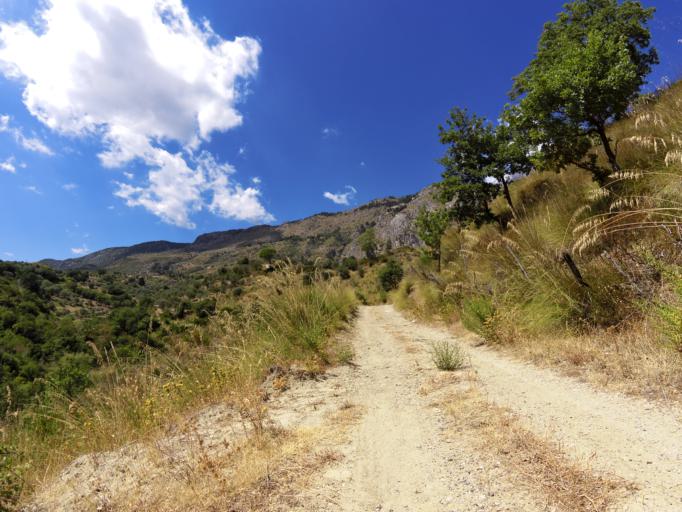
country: IT
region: Calabria
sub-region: Provincia di Reggio Calabria
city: Pazzano
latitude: 38.4637
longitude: 16.4589
